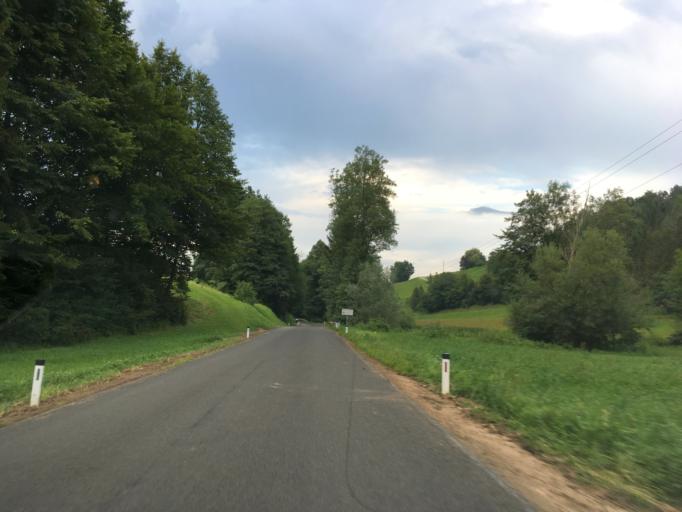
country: AT
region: Styria
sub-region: Politischer Bezirk Leibnitz
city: Oberhaag
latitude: 46.6753
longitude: 15.3516
